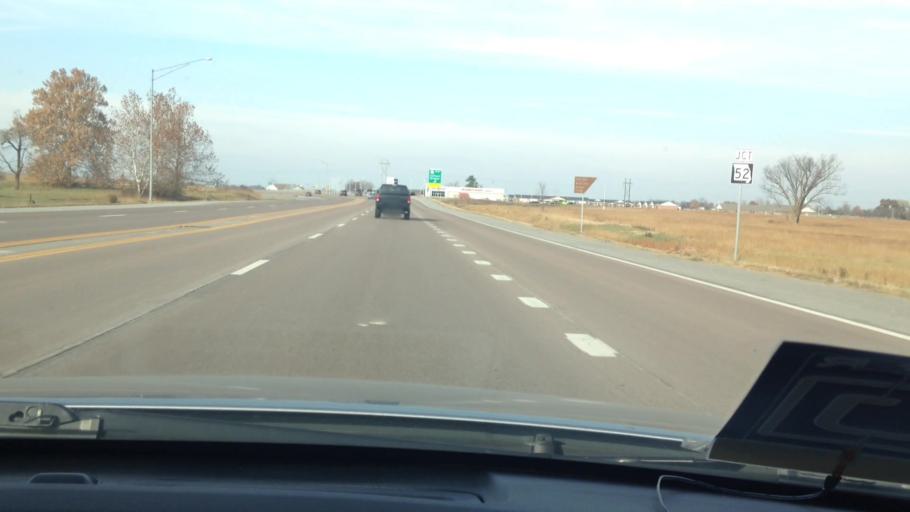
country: US
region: Missouri
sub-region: Henry County
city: Clinton
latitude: 38.3792
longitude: -93.7515
